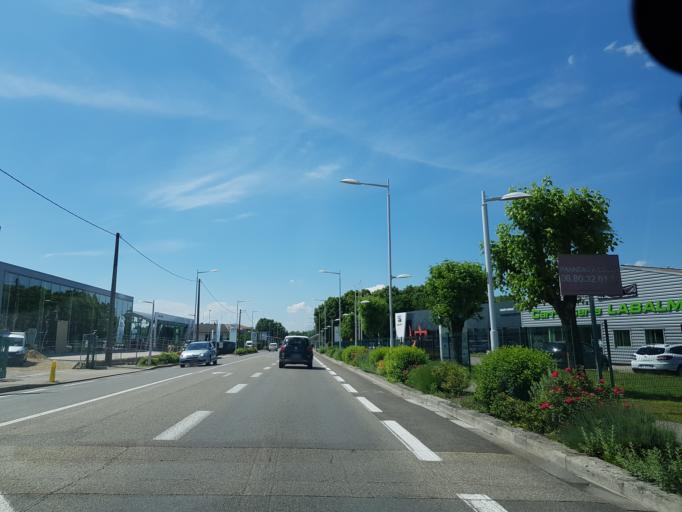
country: FR
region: Rhone-Alpes
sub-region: Departement de l'Ain
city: Bourg-en-Bresse
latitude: 46.1994
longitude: 5.2562
